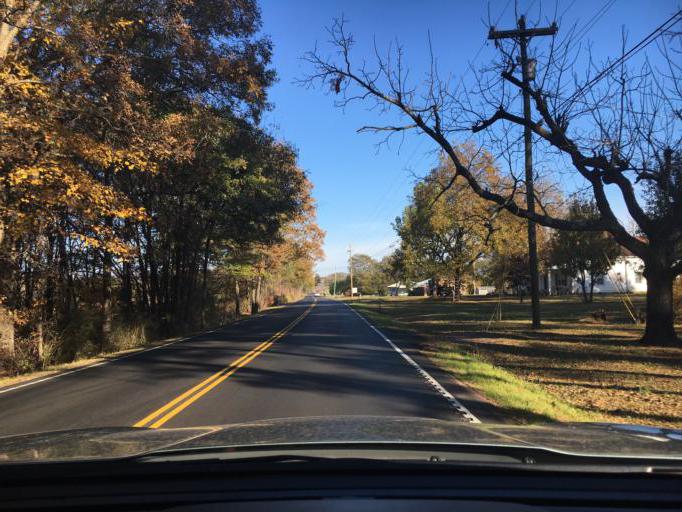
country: US
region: South Carolina
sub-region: Spartanburg County
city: Inman Mills
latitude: 35.0299
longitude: -82.1139
